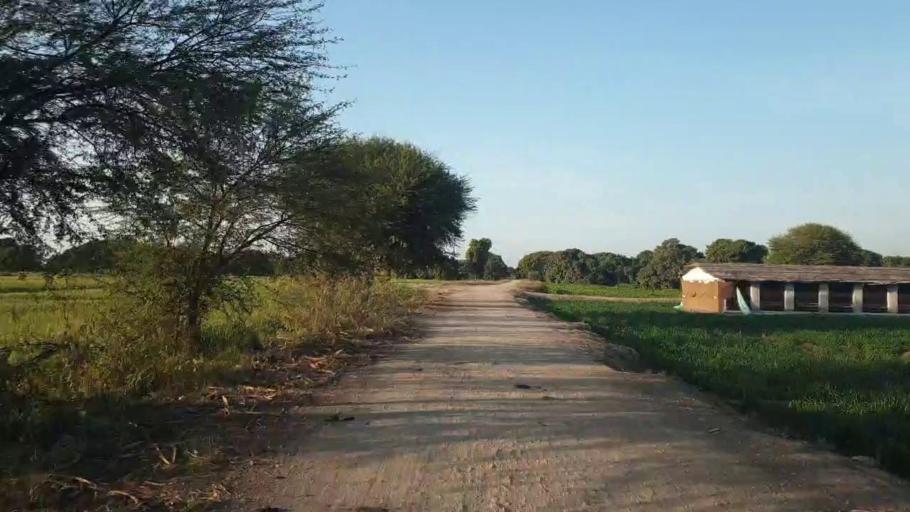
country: PK
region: Sindh
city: Chambar
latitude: 25.2732
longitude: 68.7725
